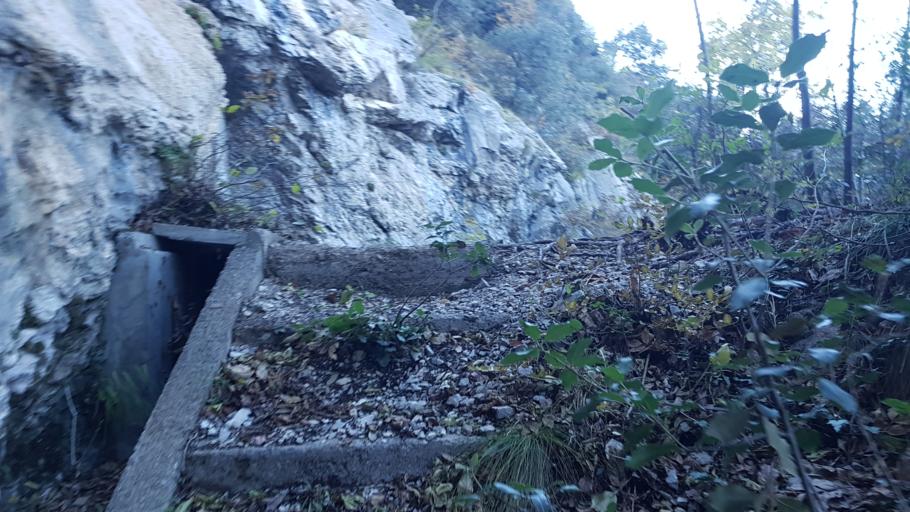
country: IT
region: Trentino-Alto Adige
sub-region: Provincia di Trento
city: Padergnone
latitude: 46.0720
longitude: 10.9796
